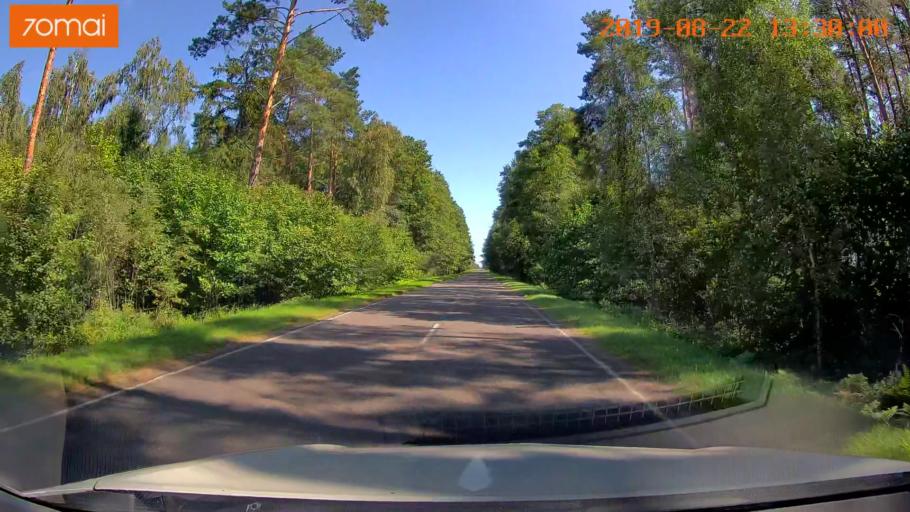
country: BY
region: Minsk
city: Staryya Darohi
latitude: 53.2173
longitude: 28.1454
